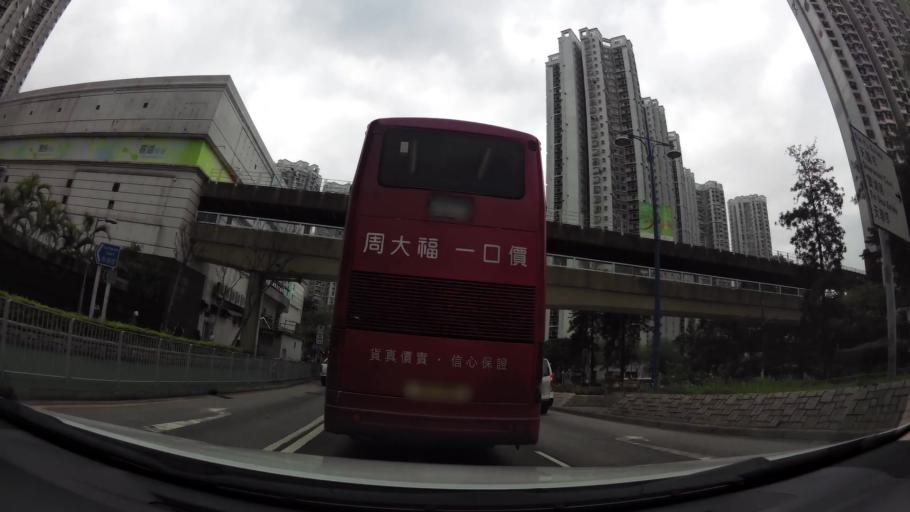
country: HK
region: Yuen Long
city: Yuen Long Kau Hui
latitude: 22.4515
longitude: 114.0018
